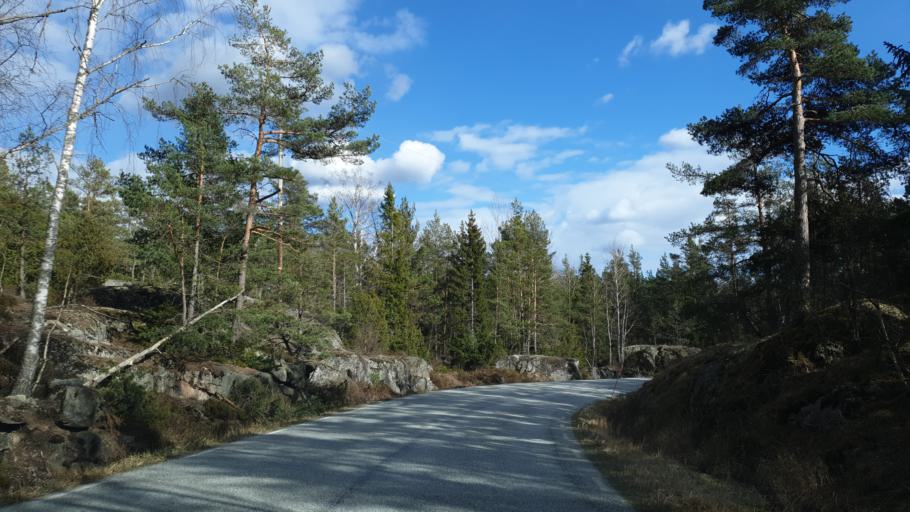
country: SE
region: Stockholm
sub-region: Varmdo Kommun
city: Hemmesta
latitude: 59.2402
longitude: 18.4752
